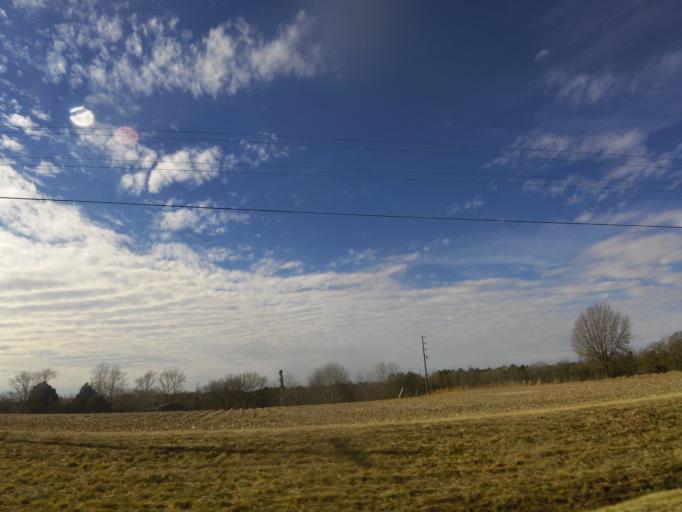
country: US
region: Virginia
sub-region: City of Franklin
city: Franklin
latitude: 36.7415
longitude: -76.8762
